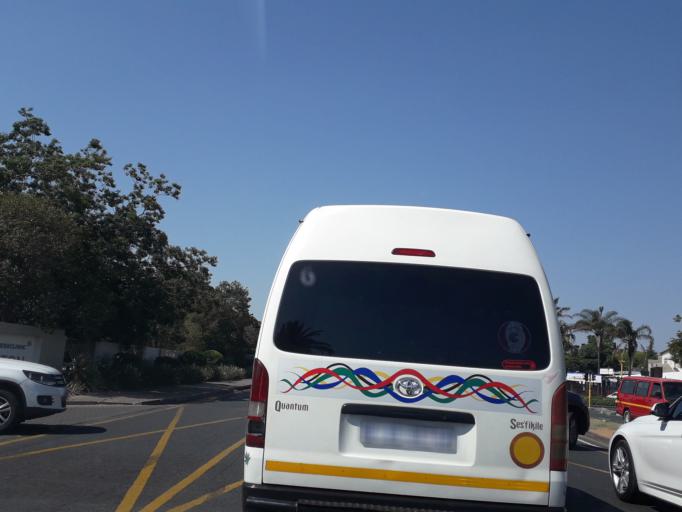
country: ZA
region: Gauteng
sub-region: City of Johannesburg Metropolitan Municipality
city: Johannesburg
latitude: -26.0769
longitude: 28.0115
